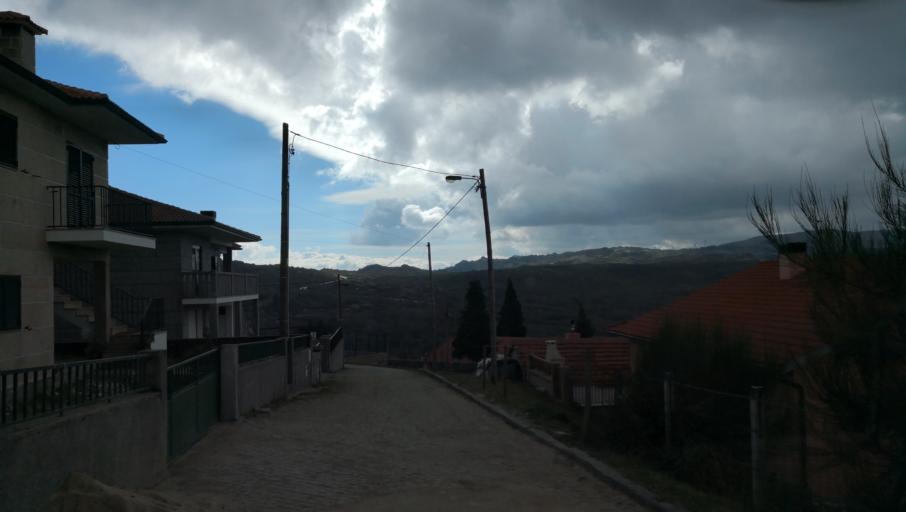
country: PT
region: Vila Real
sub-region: Vila Real
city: Vila Real
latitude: 41.3713
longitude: -7.7931
